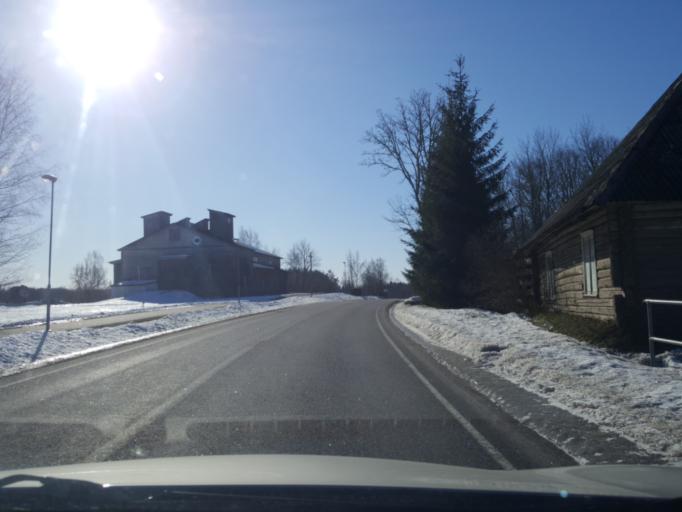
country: EE
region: Viljandimaa
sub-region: Viiratsi vald
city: Viiratsi
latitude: 58.4278
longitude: 25.6839
